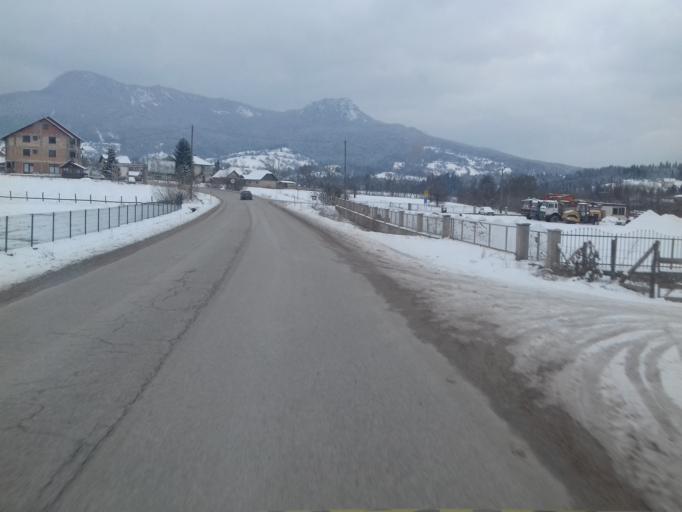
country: BA
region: Republika Srpska
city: Pale
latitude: 43.8729
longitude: 18.5839
